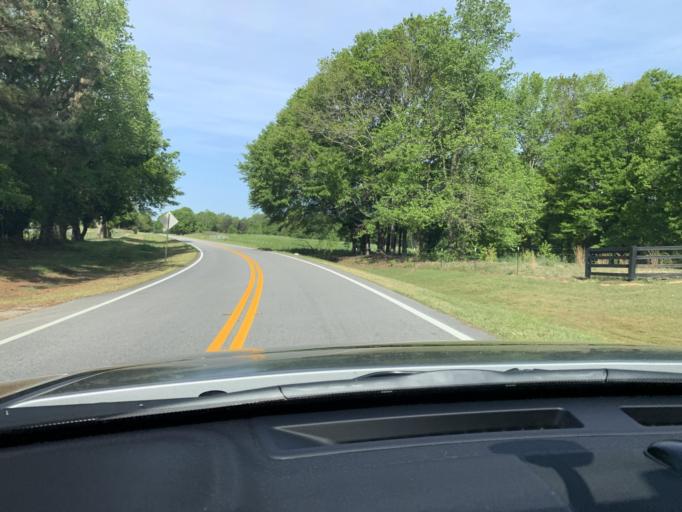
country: US
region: Georgia
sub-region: Oconee County
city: Watkinsville
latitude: 33.8137
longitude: -83.4073
